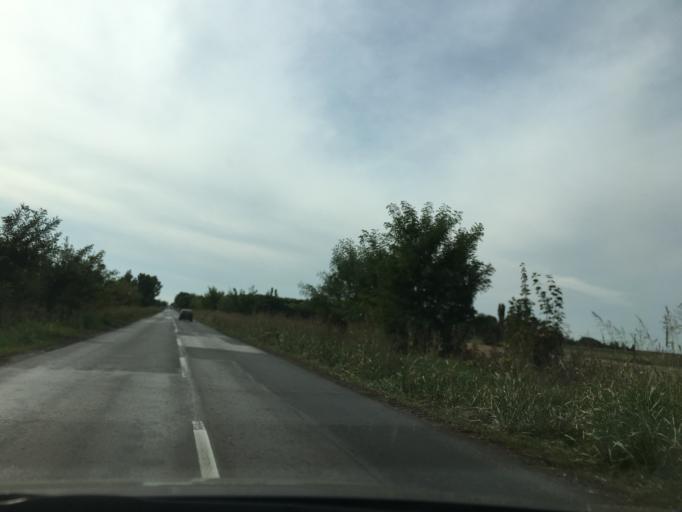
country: RS
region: Autonomna Pokrajina Vojvodina
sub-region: Juznobacki Okrug
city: Temerin
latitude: 45.4613
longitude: 19.9117
